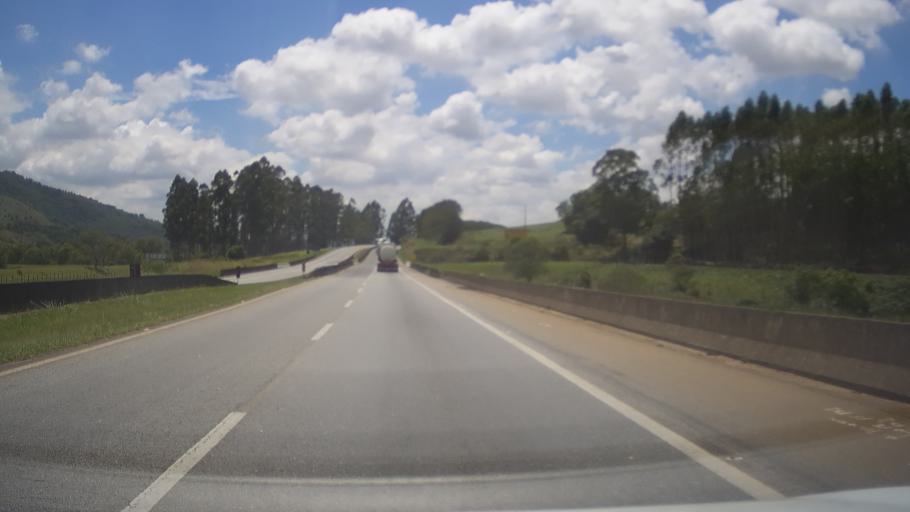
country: BR
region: Minas Gerais
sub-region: Campanha
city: Campanha
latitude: -21.8083
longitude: -45.4815
